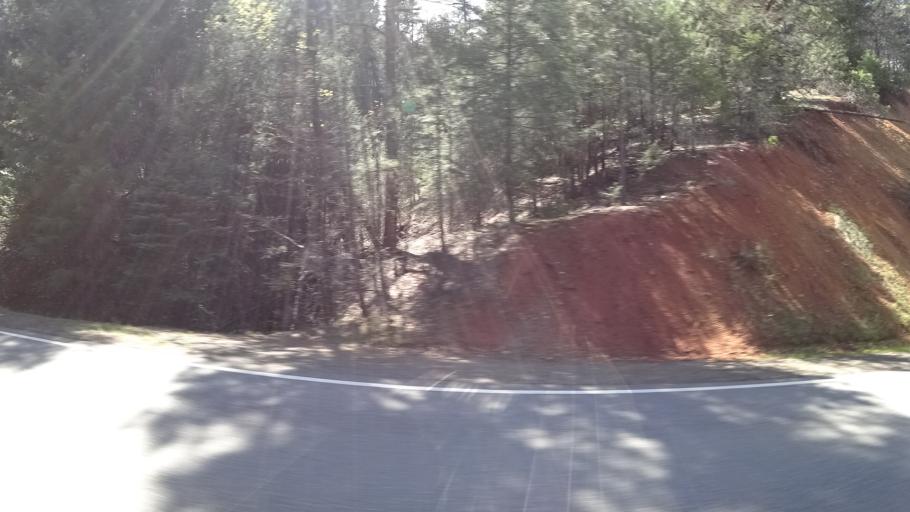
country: US
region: California
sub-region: Trinity County
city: Weaverville
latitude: 40.7977
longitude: -122.8886
